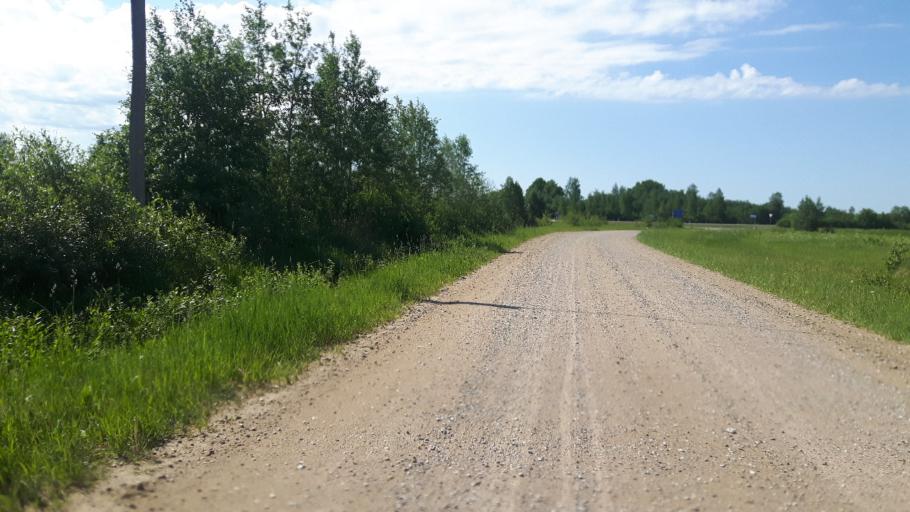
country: EE
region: Paernumaa
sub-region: Vaendra vald (alev)
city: Vandra
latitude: 58.6643
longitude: 25.0247
